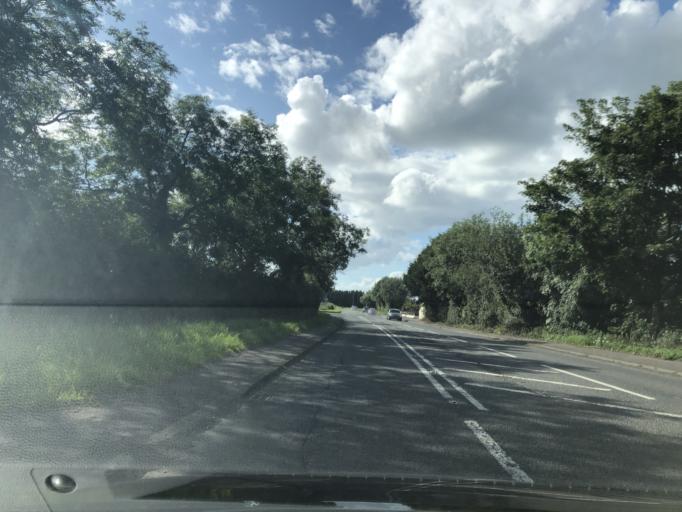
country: GB
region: Northern Ireland
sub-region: Ards District
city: Comber
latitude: 54.5690
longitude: -5.7704
